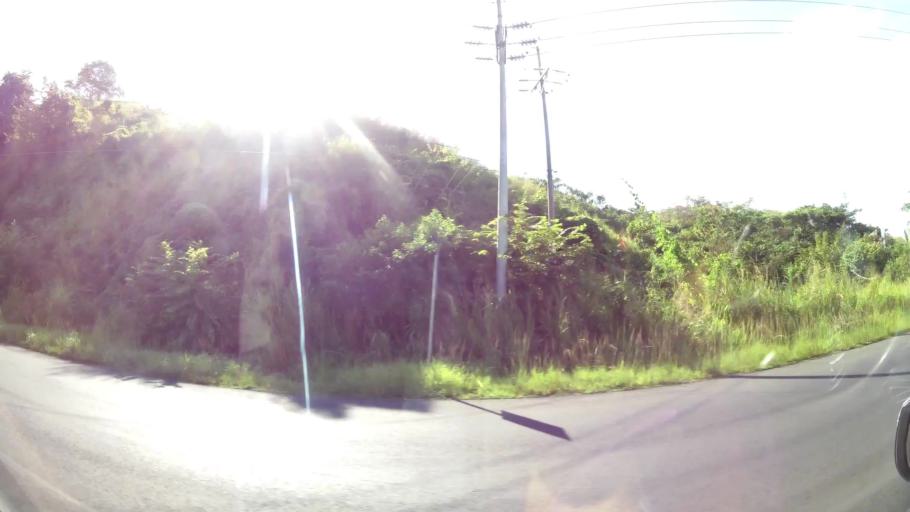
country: CR
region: Puntarenas
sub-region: Canton de Garabito
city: Jaco
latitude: 9.6412
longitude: -84.6274
